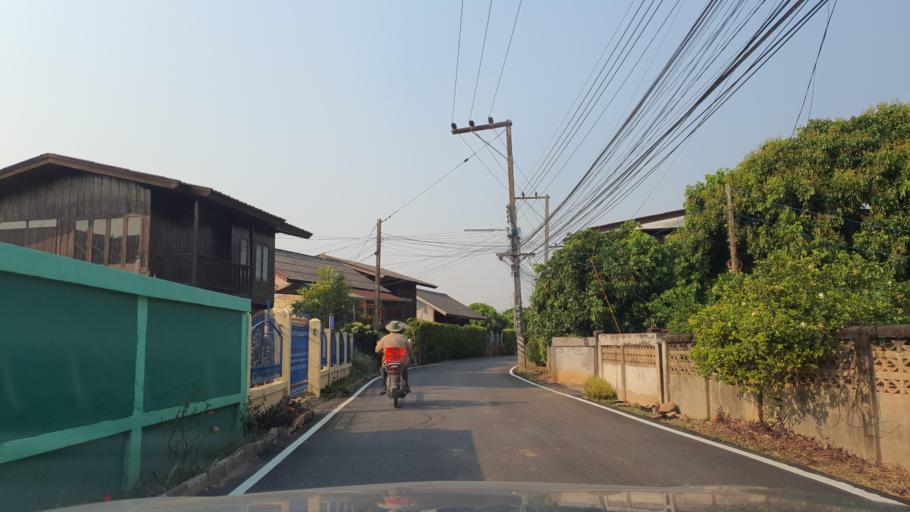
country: TH
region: Chiang Mai
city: Mae Taeng
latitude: 19.1364
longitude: 99.0094
